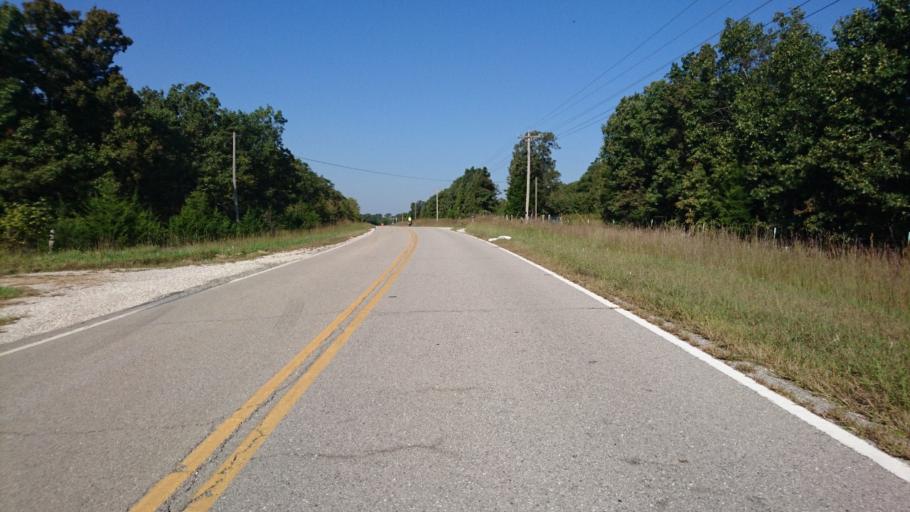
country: US
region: Missouri
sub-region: Pulaski County
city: Richland
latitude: 37.7509
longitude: -92.3637
